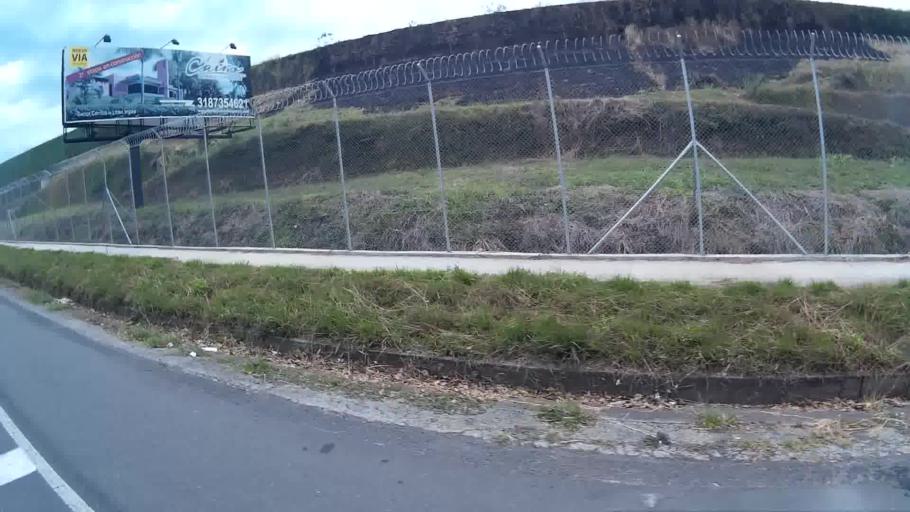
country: CO
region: Risaralda
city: Pereira
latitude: 4.8088
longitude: -75.7473
